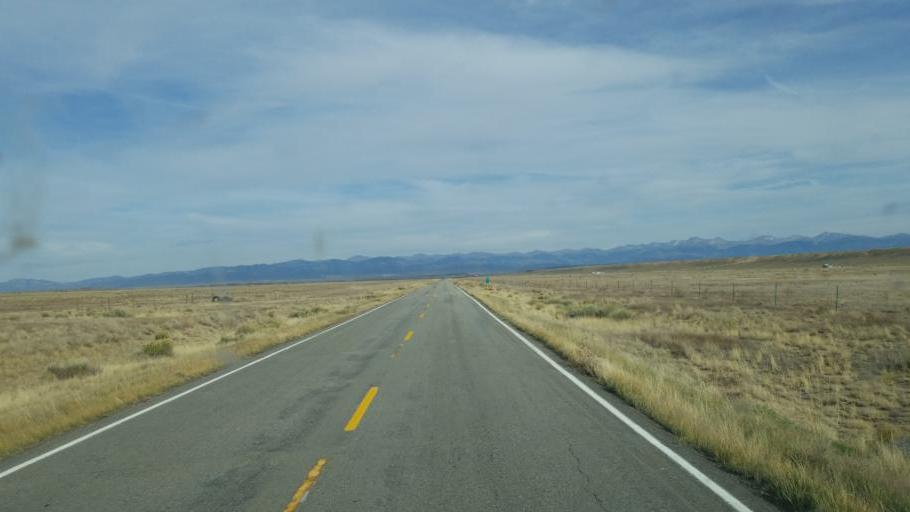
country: US
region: Colorado
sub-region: Costilla County
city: San Luis
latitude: 37.1821
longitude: -105.6131
